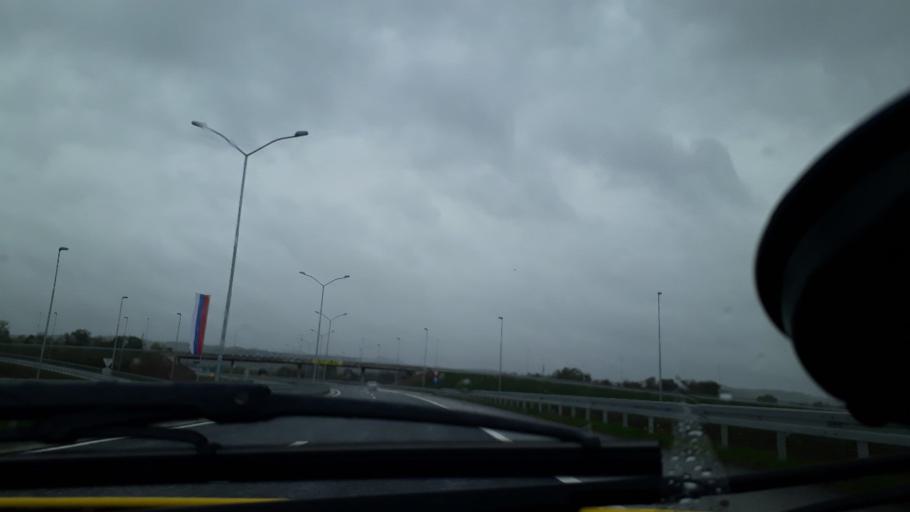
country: BA
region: Republika Srpska
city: Laktasi
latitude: 44.9191
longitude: 17.3274
